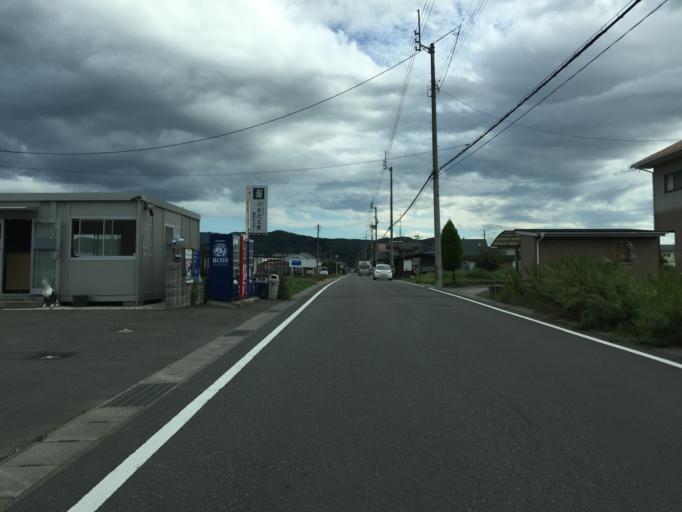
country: JP
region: Fukushima
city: Fukushima-shi
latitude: 37.7838
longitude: 140.4961
